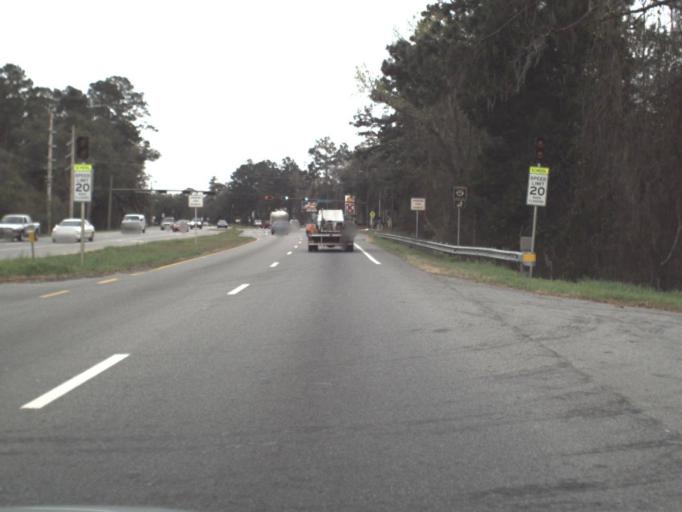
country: US
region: Florida
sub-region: Leon County
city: Tallahassee
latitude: 30.5126
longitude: -84.3440
